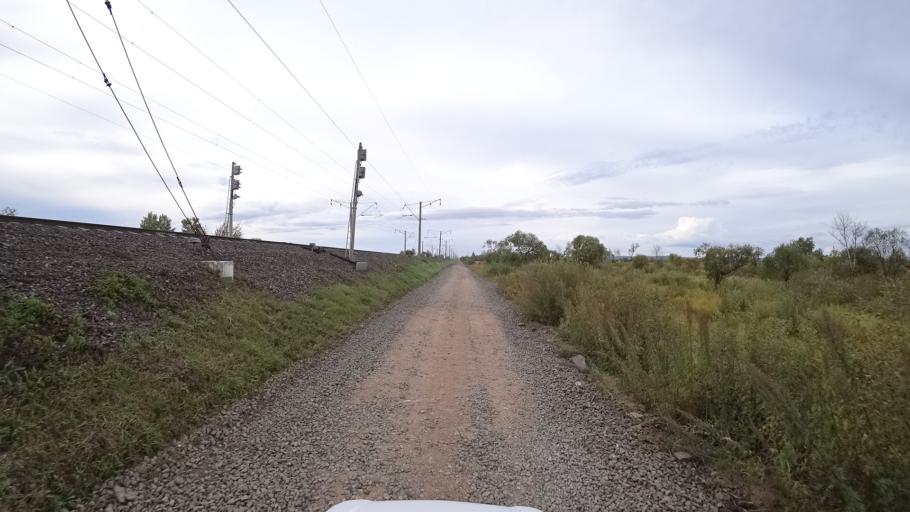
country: RU
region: Amur
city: Arkhara
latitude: 49.3573
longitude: 130.1529
